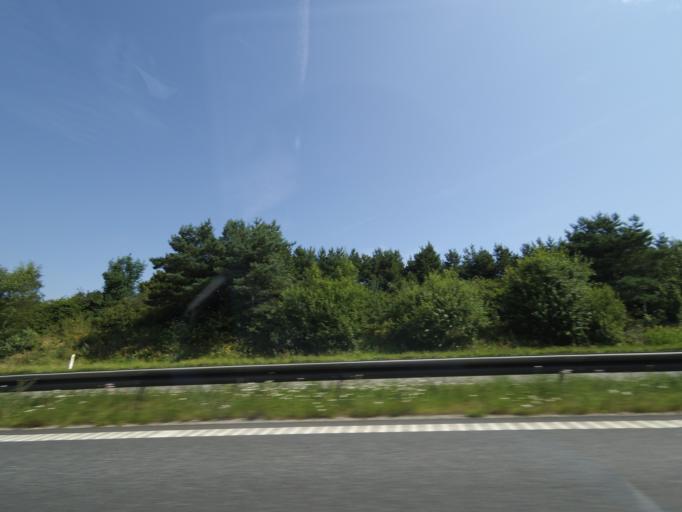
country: DK
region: South Denmark
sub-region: Fredericia Kommune
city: Taulov
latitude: 55.5578
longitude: 9.6290
